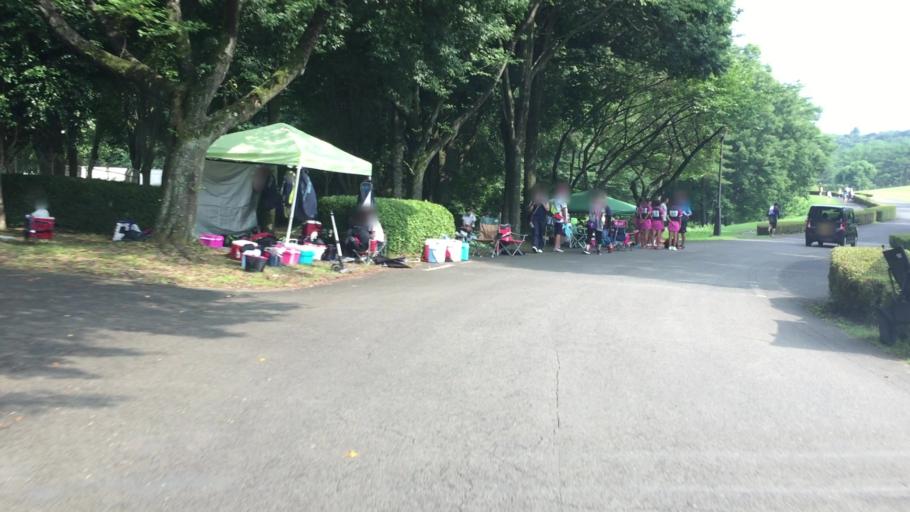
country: JP
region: Tochigi
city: Otawara
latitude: 36.9292
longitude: 139.9521
